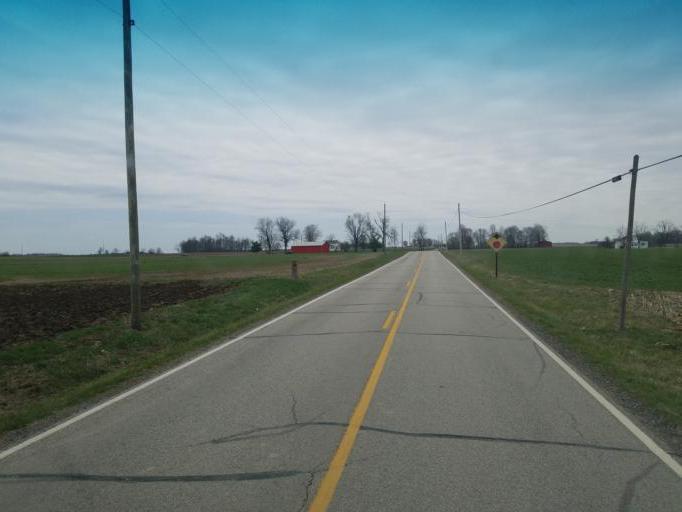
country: US
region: Ohio
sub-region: Crawford County
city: Bucyrus
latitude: 40.8653
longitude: -82.9434
